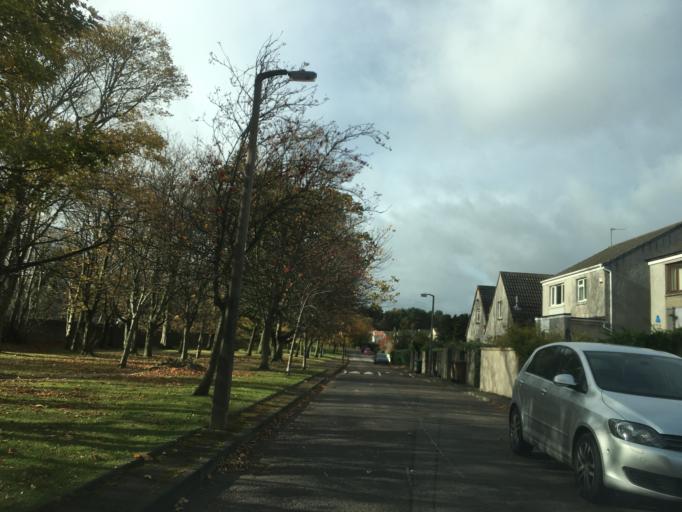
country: GB
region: Scotland
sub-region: Midlothian
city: Loanhead
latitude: 55.8998
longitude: -3.1696
